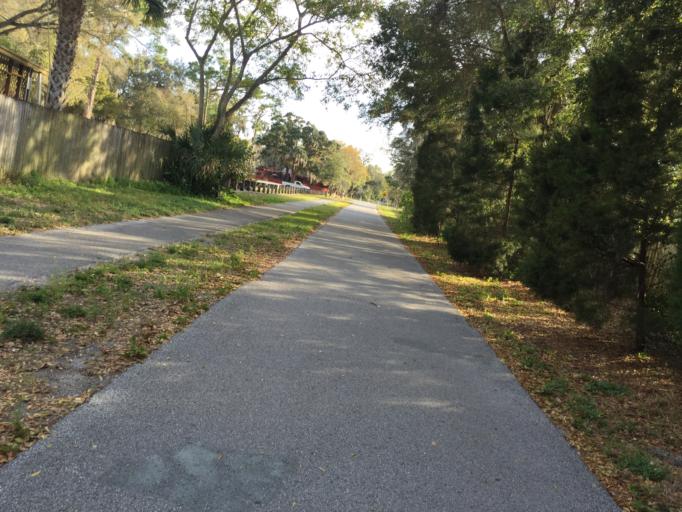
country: US
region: Florida
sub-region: Pinellas County
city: Clearwater
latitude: 27.9937
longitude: -82.7895
